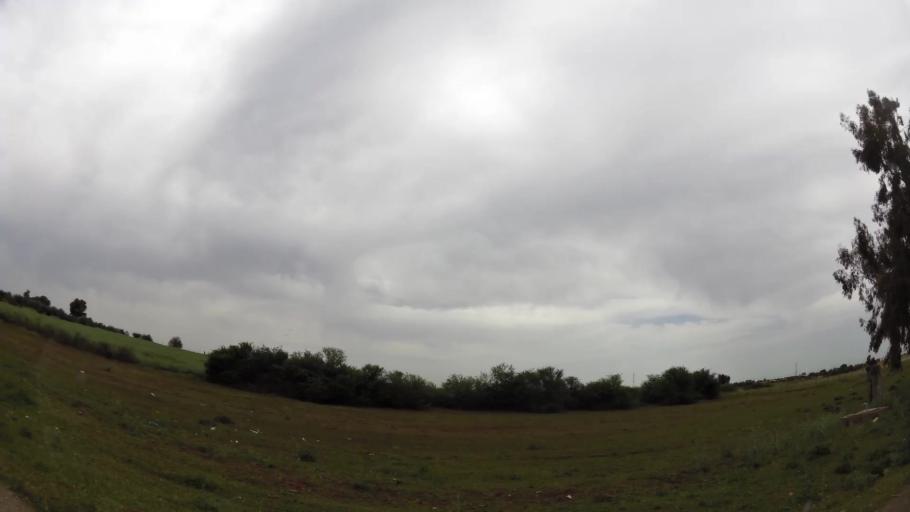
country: MA
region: Rabat-Sale-Zemmour-Zaer
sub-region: Khemisset
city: Tiflet
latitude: 33.8325
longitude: -6.2718
